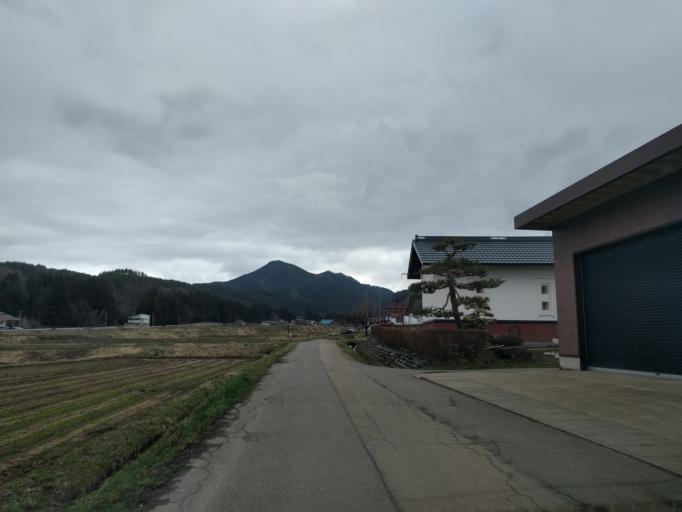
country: JP
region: Fukushima
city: Kitakata
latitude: 37.6682
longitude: 139.9167
